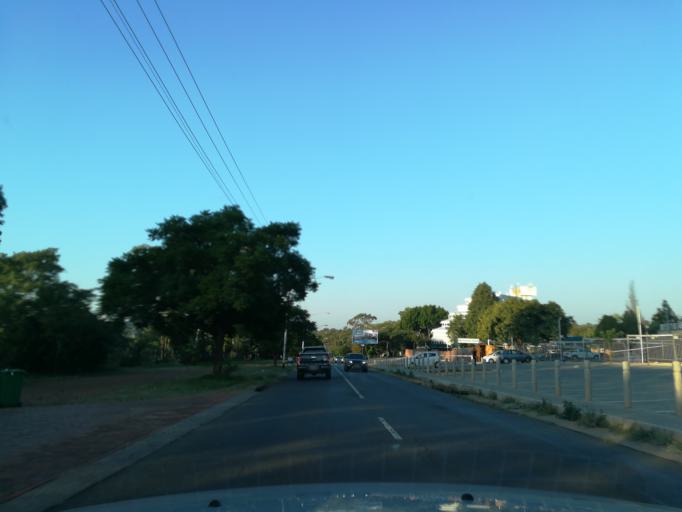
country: ZA
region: Gauteng
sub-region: City of Tshwane Metropolitan Municipality
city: Pretoria
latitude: -25.7701
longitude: 28.2156
